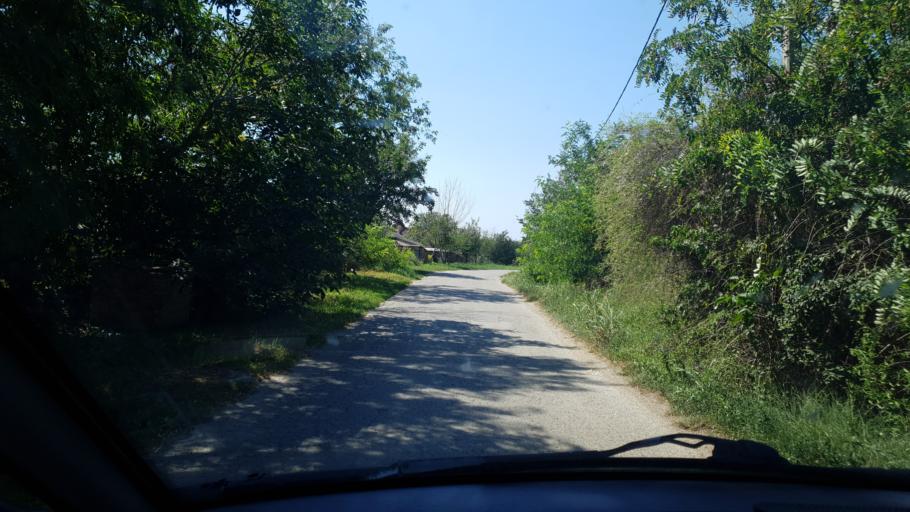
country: RS
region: Autonomna Pokrajina Vojvodina
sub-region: Juznobacki Okrug
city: Kovilj
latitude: 45.2231
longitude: 20.0315
